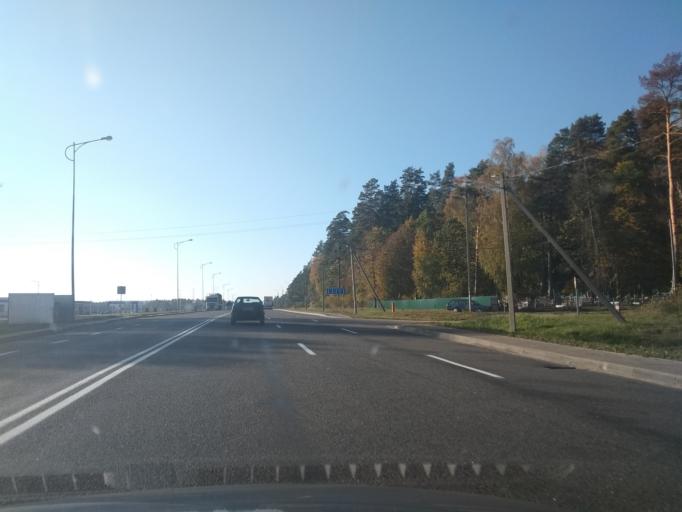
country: BY
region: Grodnenskaya
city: Vyalikaya Byerastavitsa
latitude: 53.1208
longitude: 23.9152
